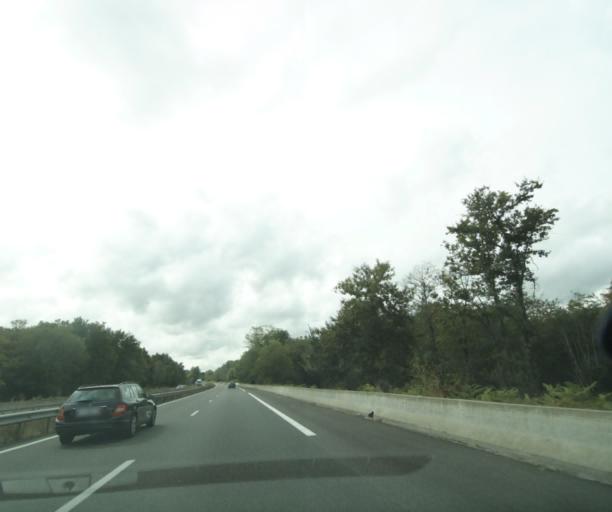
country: FR
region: Poitou-Charentes
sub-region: Departement de la Charente-Maritime
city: Saint-Genis-de-Saintonge
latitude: 45.4797
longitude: -0.6192
